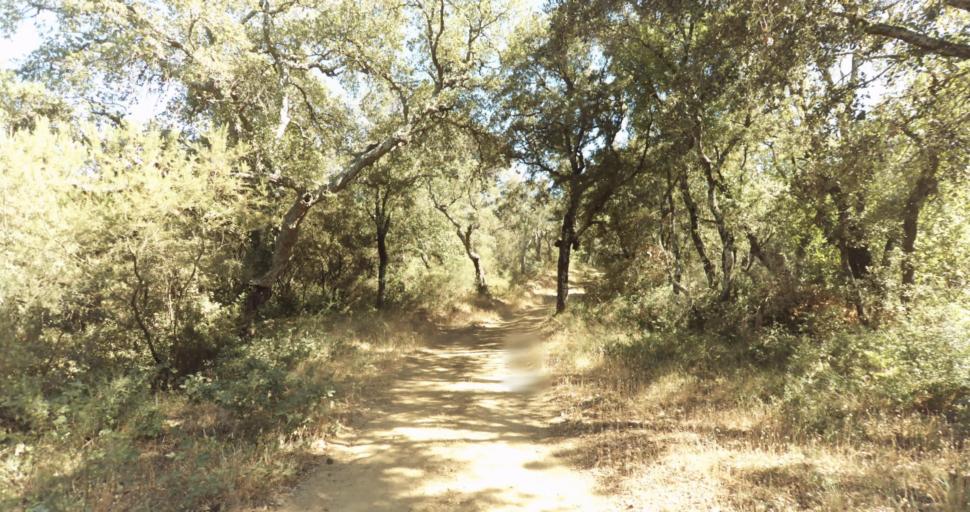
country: FR
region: Provence-Alpes-Cote d'Azur
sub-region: Departement du Var
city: Gassin
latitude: 43.2456
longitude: 6.5845
